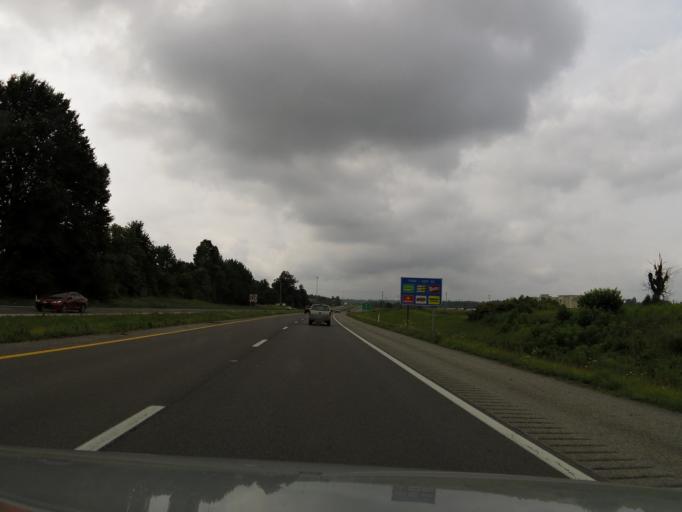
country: US
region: Kentucky
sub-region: Hopkins County
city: Madisonville
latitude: 37.3338
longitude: -87.4771
